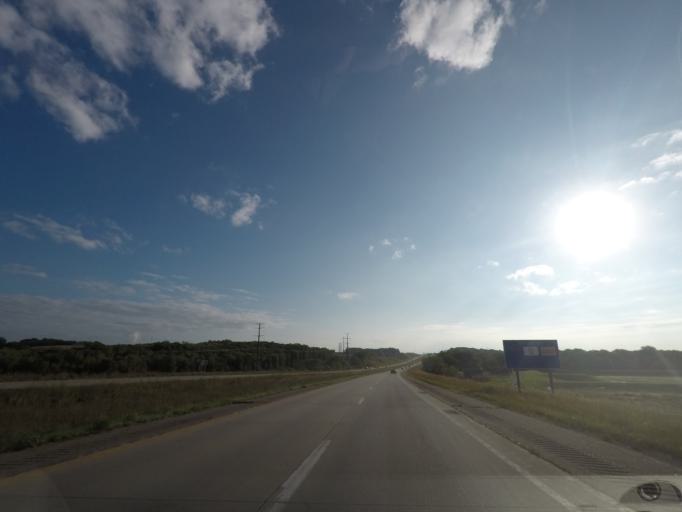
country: US
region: Iowa
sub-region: Warren County
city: Norwalk
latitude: 41.5025
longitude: -93.5926
